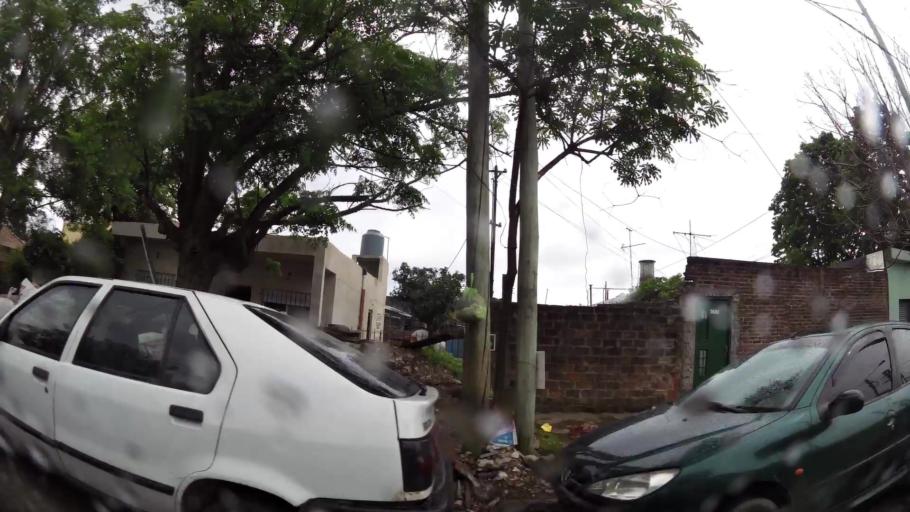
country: AR
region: Buenos Aires
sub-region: Partido de Quilmes
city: Quilmes
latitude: -34.7631
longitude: -58.2250
